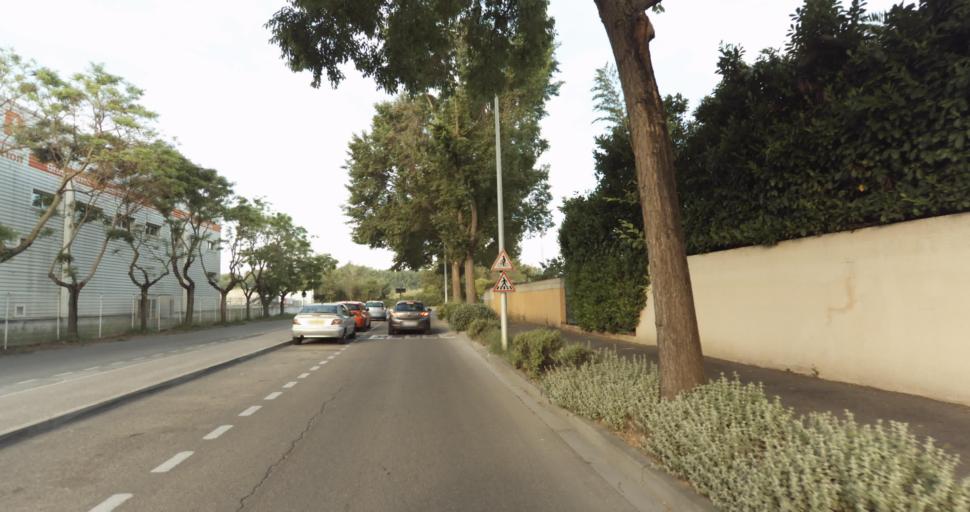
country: FR
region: Languedoc-Roussillon
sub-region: Departement du Gard
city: Caissargues
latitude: 43.8253
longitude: 4.3822
